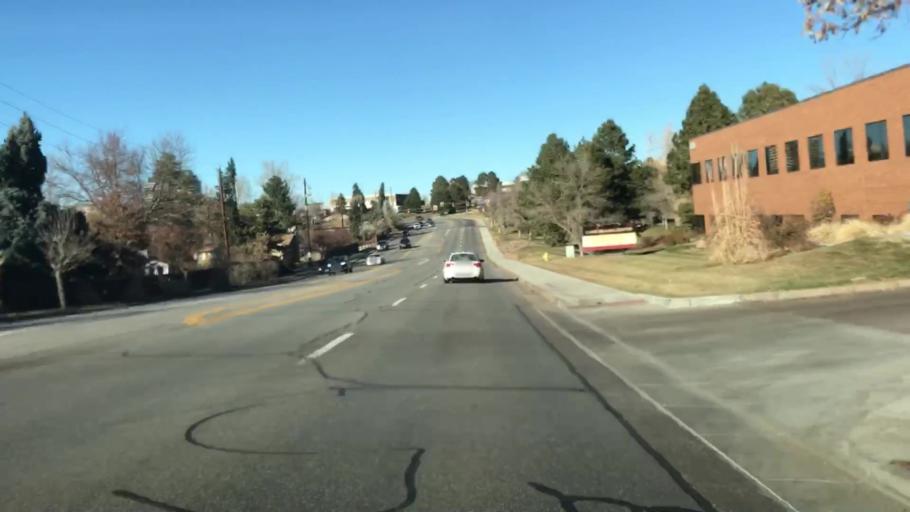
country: US
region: Colorado
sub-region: Arapahoe County
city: Centennial
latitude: 39.5884
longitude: -104.8853
